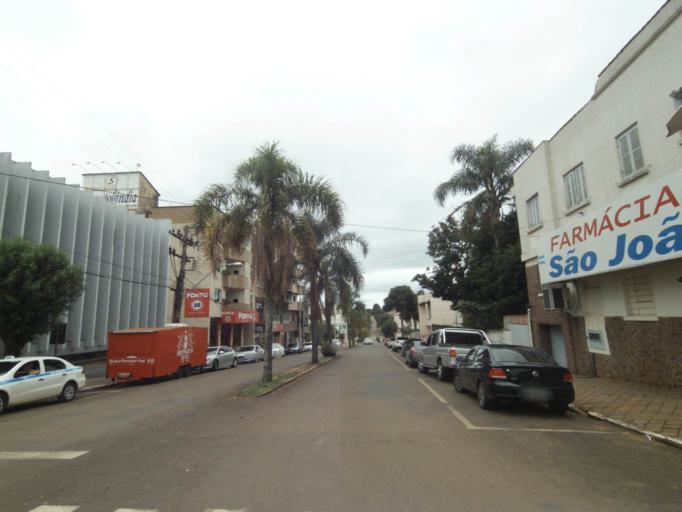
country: BR
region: Rio Grande do Sul
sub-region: Lagoa Vermelha
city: Lagoa Vermelha
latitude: -28.2101
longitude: -51.5230
